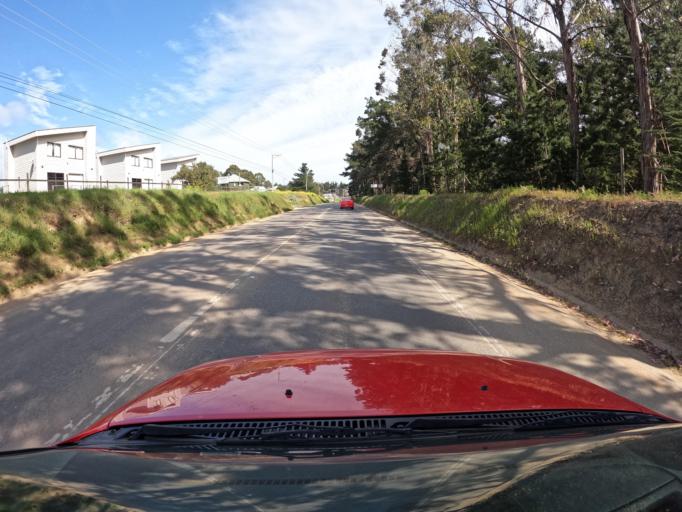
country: CL
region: O'Higgins
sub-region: Provincia de Colchagua
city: Santa Cruz
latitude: -34.4235
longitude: -72.0309
